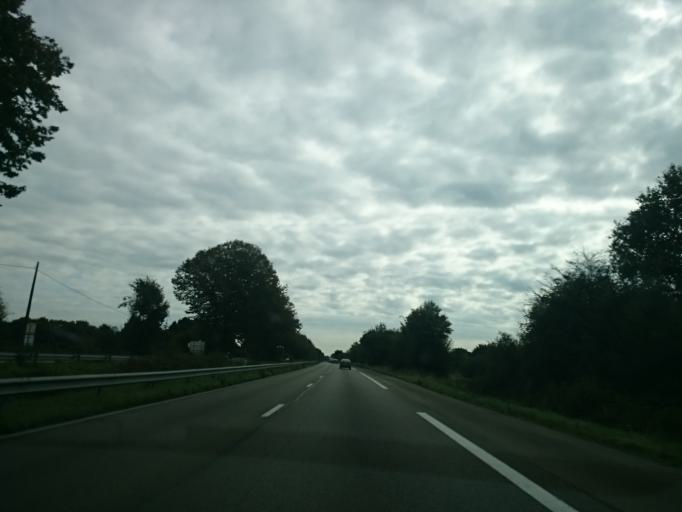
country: FR
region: Pays de la Loire
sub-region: Departement de la Loire-Atlantique
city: Malville
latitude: 47.3450
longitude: -1.8584
